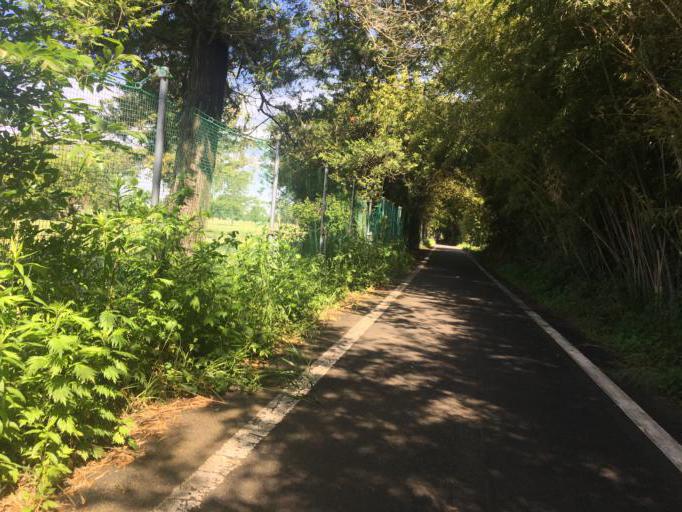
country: JP
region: Saitama
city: Shiki
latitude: 35.8619
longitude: 139.5869
